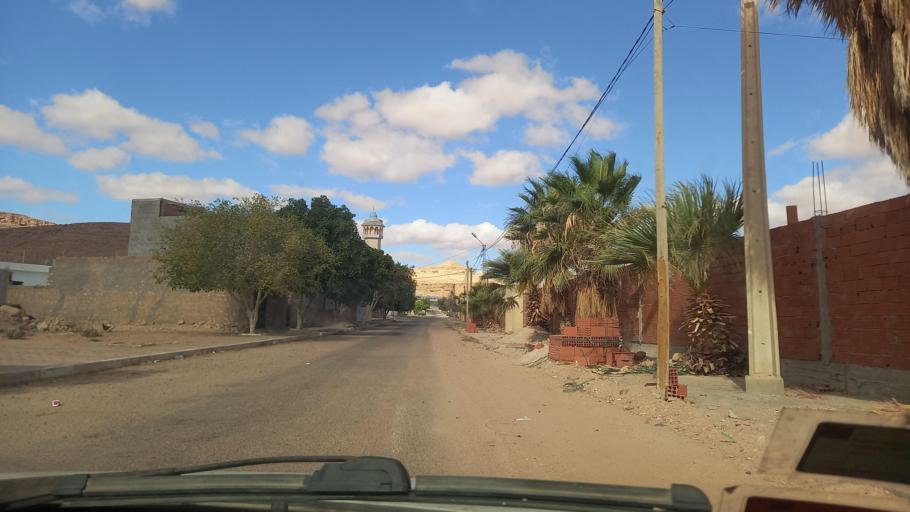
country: TN
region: Tataouine
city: Tataouine
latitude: 32.9801
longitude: 10.2691
